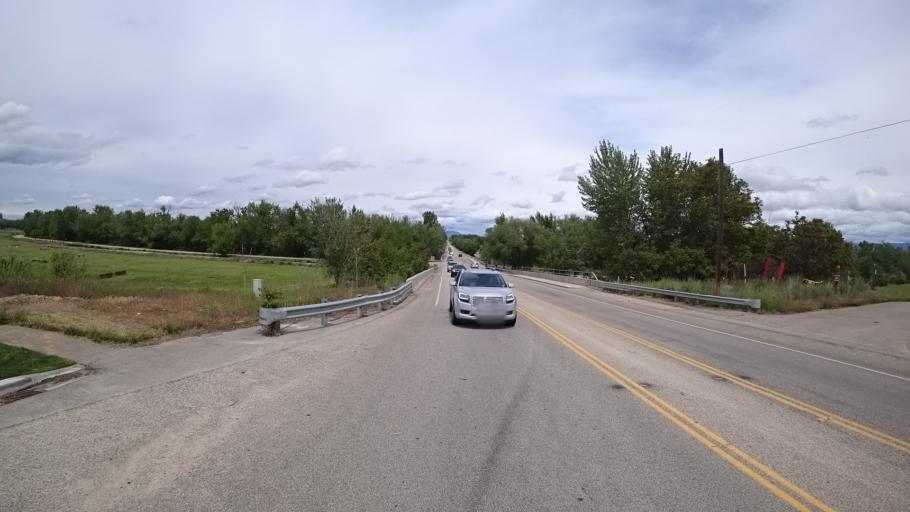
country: US
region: Idaho
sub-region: Ada County
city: Eagle
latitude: 43.6723
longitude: -116.4138
